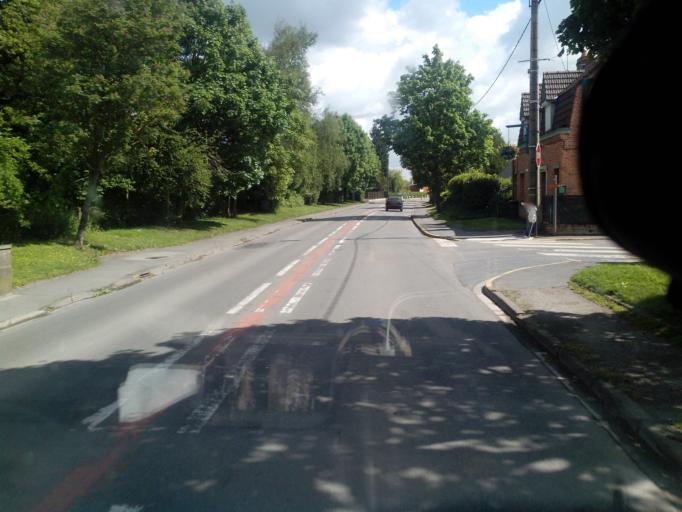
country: FR
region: Nord-Pas-de-Calais
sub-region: Departement du Pas-de-Calais
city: Sailly-sur-la-Lys
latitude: 50.6608
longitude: 2.7747
